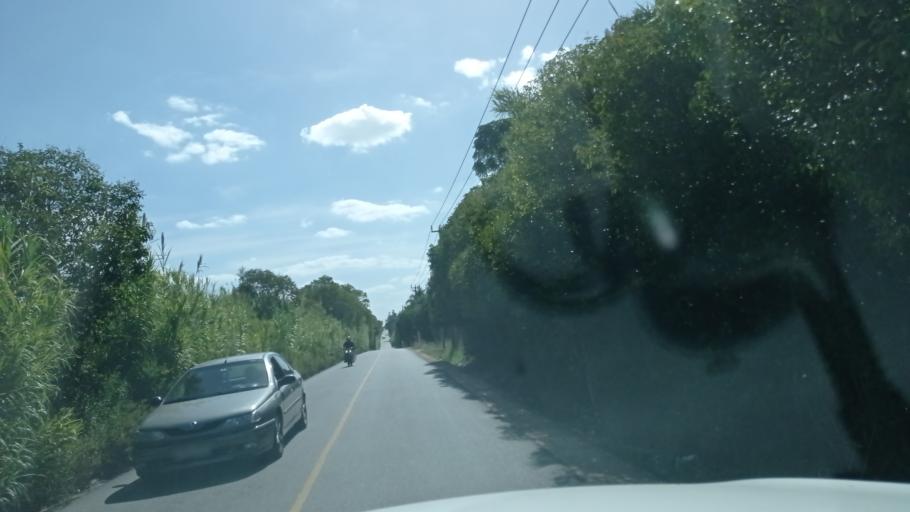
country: UY
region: Canelones
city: La Paz
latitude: -34.8056
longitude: -56.2054
